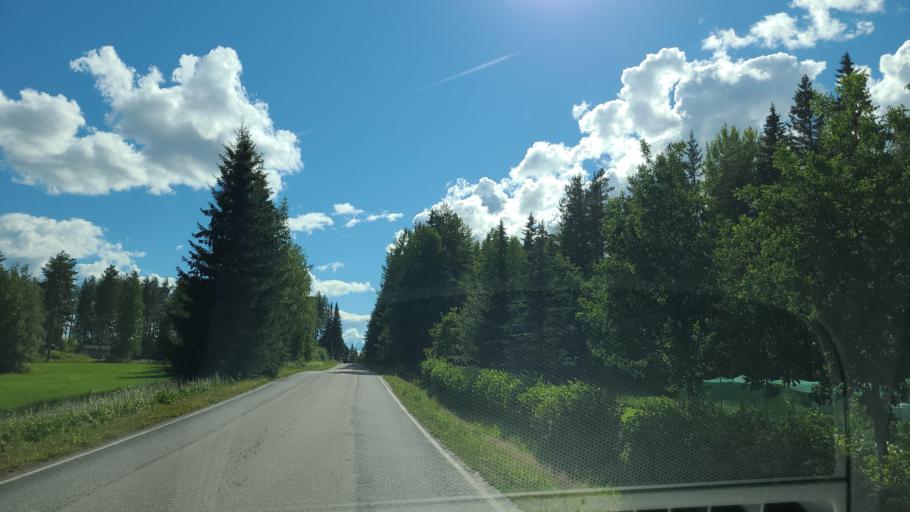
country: FI
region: Central Finland
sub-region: Jaemsae
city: Jaemsae
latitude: 61.8819
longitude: 25.2302
